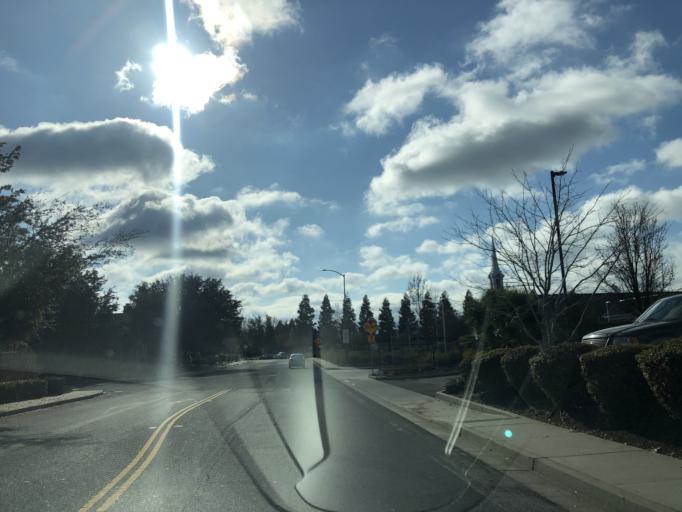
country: US
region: California
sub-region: Contra Costa County
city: Brentwood
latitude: 37.9432
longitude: -121.7342
